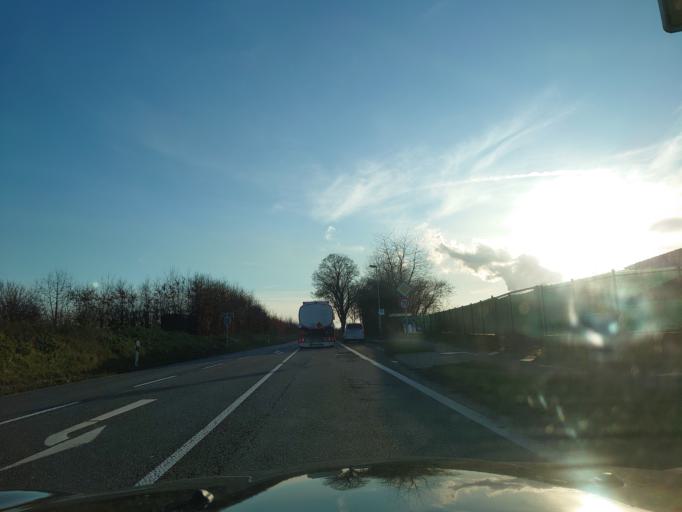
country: DE
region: North Rhine-Westphalia
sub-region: Regierungsbezirk Dusseldorf
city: Rommerskirchen
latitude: 51.0617
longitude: 6.7198
